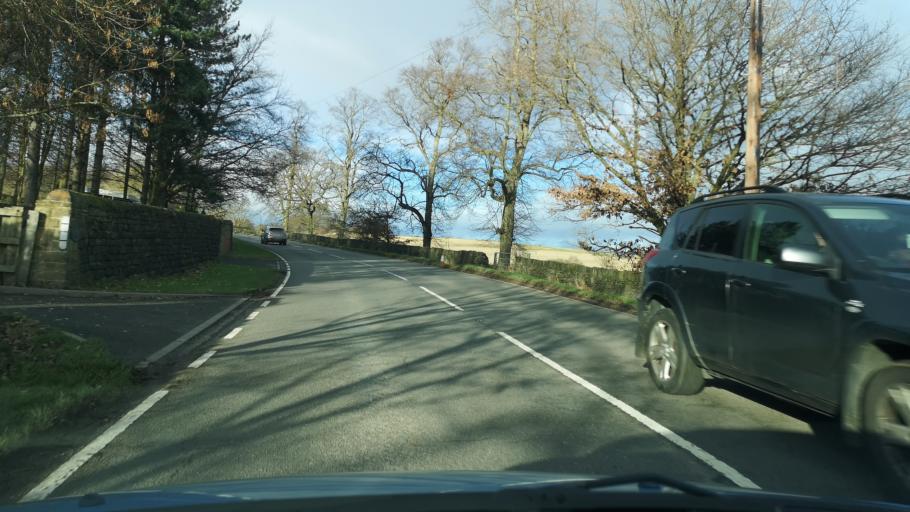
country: GB
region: England
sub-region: Barnsley
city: Darton
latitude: 53.6093
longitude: -1.5560
